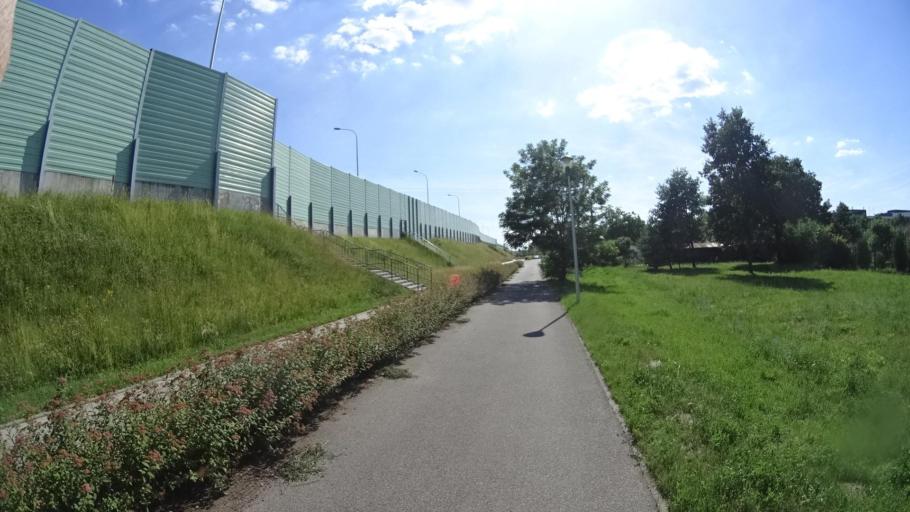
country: PL
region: Masovian Voivodeship
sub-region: Warszawa
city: Bialoleka
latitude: 52.3160
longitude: 20.9731
